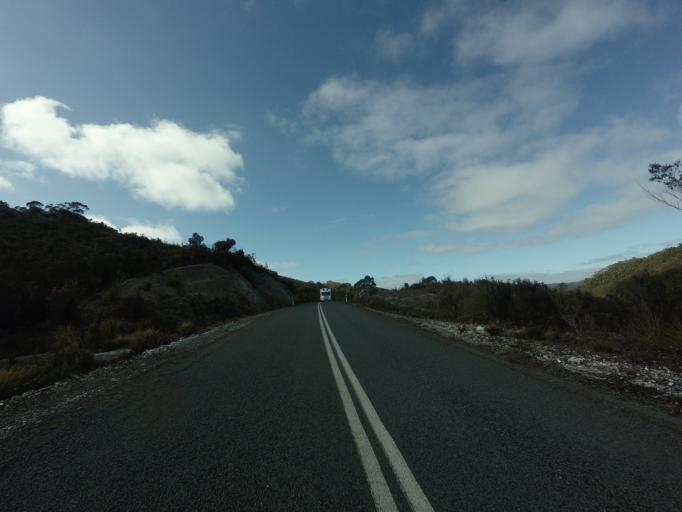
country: AU
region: Tasmania
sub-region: Huon Valley
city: Geeveston
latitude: -42.8207
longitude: 146.1234
